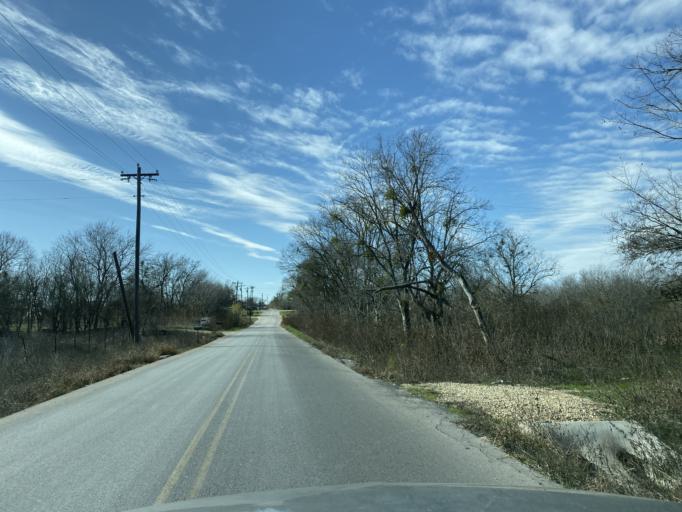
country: US
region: Texas
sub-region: Travis County
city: Onion Creek
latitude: 30.0857
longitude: -97.7010
